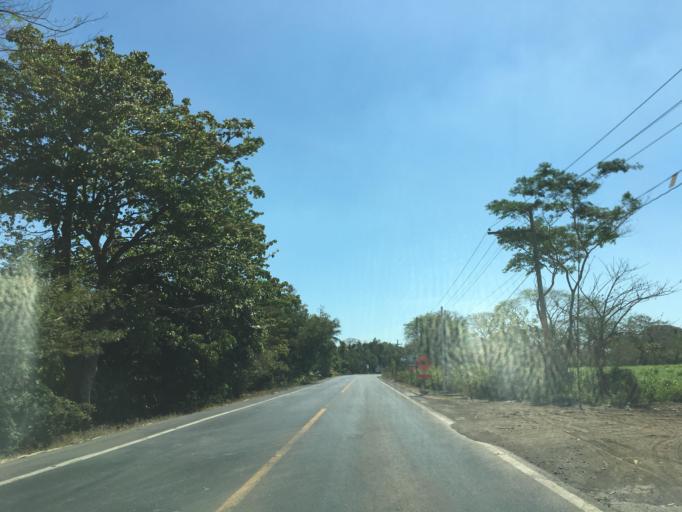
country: GT
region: Escuintla
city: Puerto San Jose
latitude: 13.9782
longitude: -90.8823
